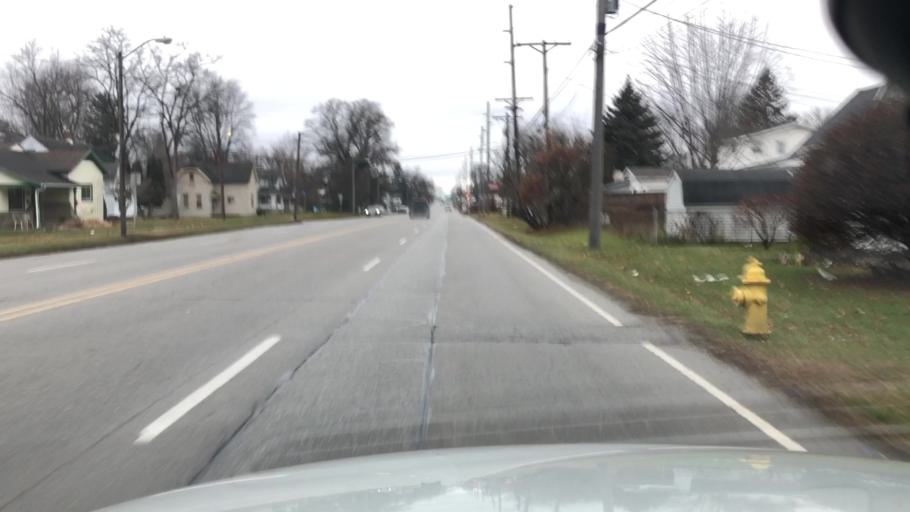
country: US
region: Indiana
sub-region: Allen County
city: New Haven
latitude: 41.0703
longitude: -85.0231
